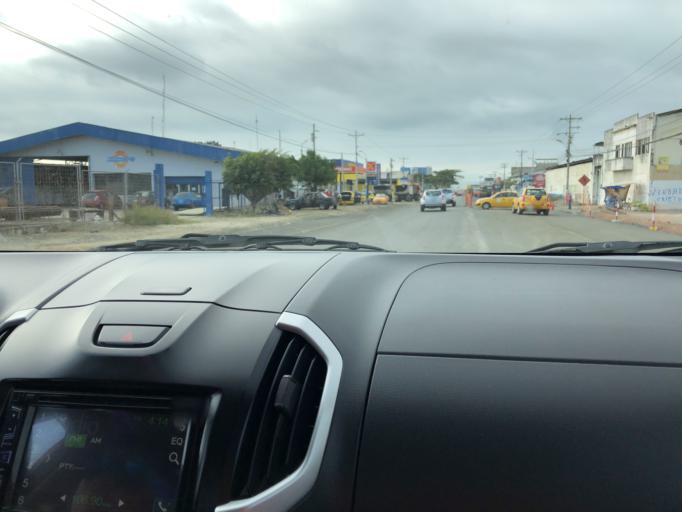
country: EC
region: Manabi
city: Manta
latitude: -0.9752
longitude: -80.6991
